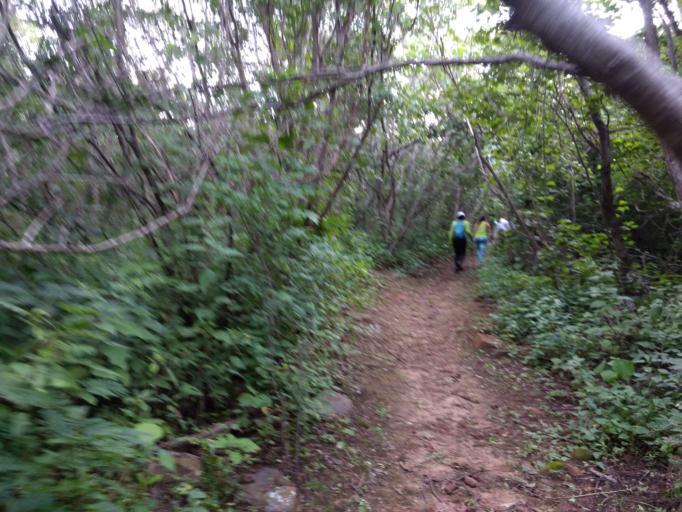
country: BR
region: Ceara
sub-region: Crateus
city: Crateus
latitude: -5.1419
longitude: -40.9192
